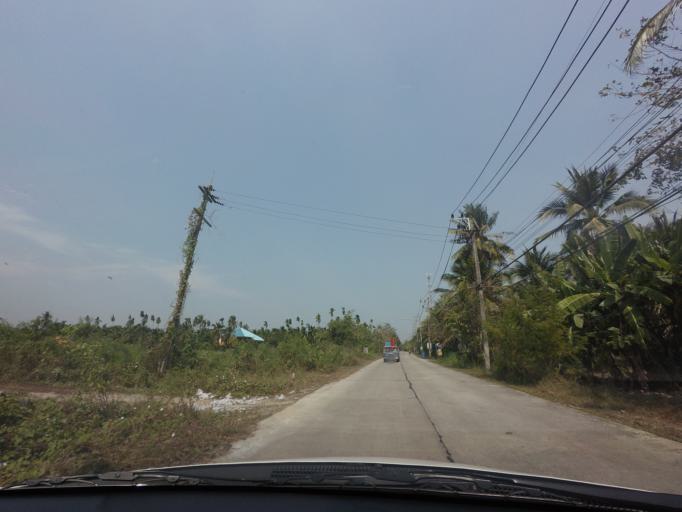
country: TH
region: Nakhon Pathom
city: Sam Phran
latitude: 13.7586
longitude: 100.2533
